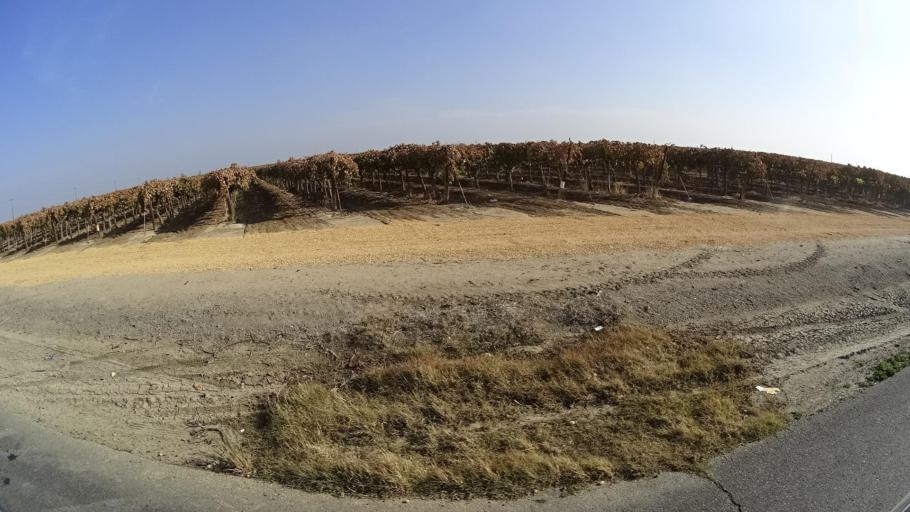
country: US
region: California
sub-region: Tulare County
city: Richgrove
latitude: 35.7313
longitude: -119.1514
